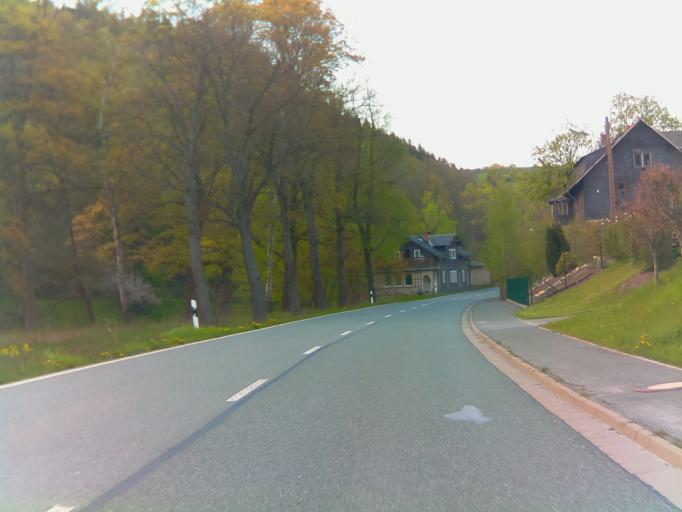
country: DE
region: Thuringia
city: Probstzella
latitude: 50.5489
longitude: 11.3482
